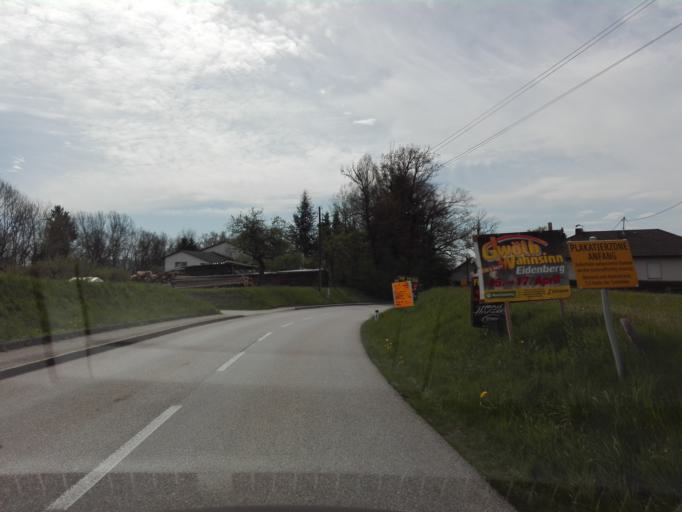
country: AT
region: Upper Austria
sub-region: Politischer Bezirk Urfahr-Umgebung
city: Walding
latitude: 48.3550
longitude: 14.1601
